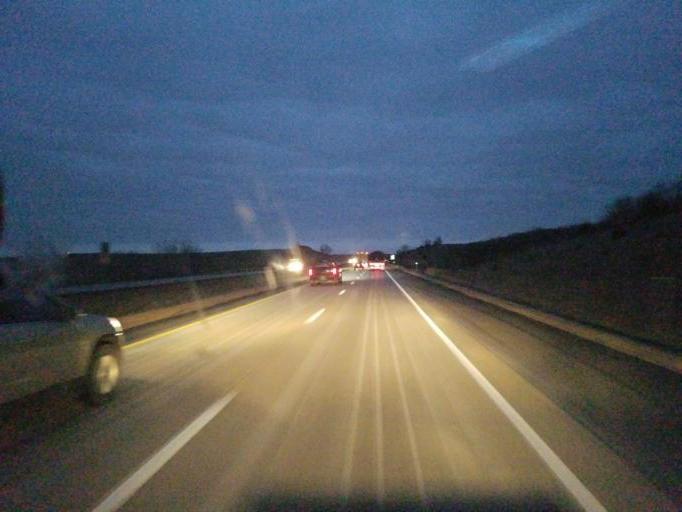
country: US
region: Iowa
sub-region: Cass County
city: Atlantic
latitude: 41.4967
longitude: -94.7721
